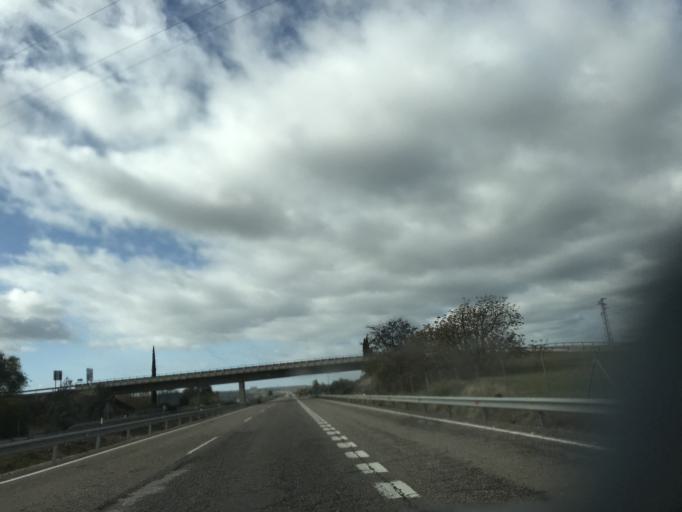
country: ES
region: Andalusia
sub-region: Provincia de Jaen
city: Andujar
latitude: 38.0306
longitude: -4.0779
